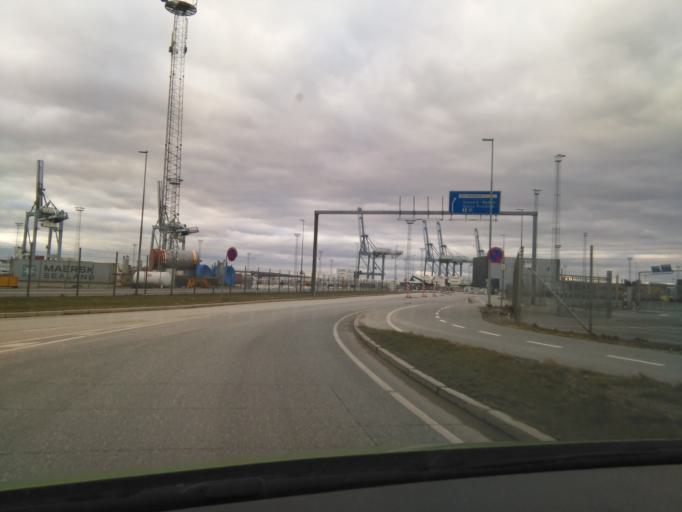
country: DK
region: Central Jutland
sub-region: Arhus Kommune
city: Arhus
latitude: 56.1464
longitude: 10.2406
